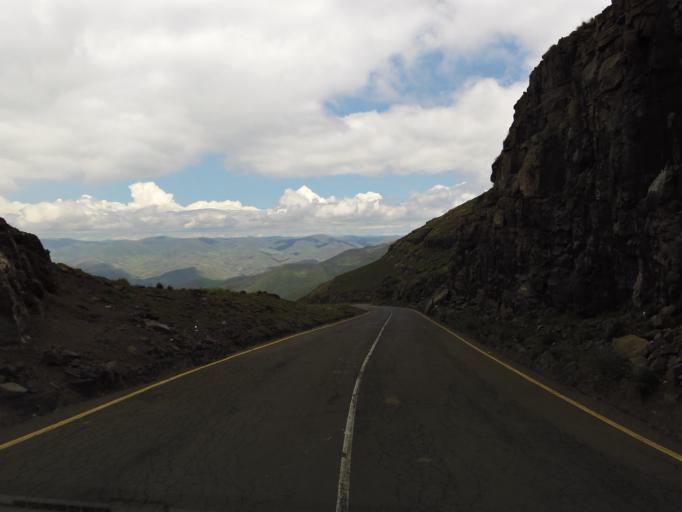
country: LS
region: Butha-Buthe
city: Butha-Buthe
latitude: -29.1034
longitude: 28.4270
